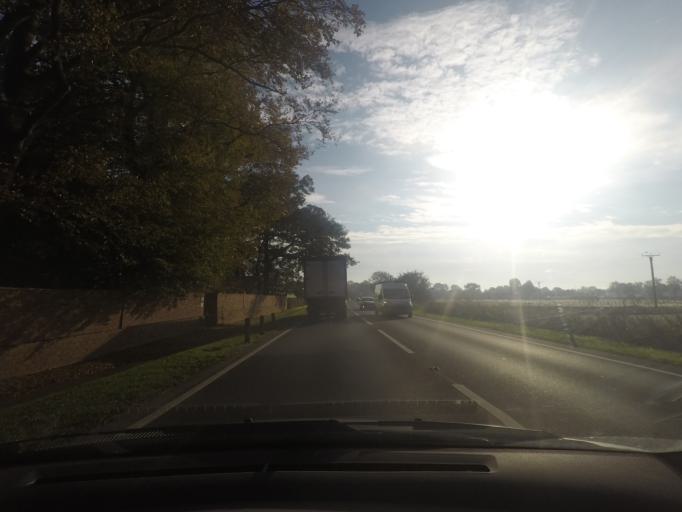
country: GB
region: England
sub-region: East Riding of Yorkshire
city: Londesborough
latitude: 53.8801
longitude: -0.7126
